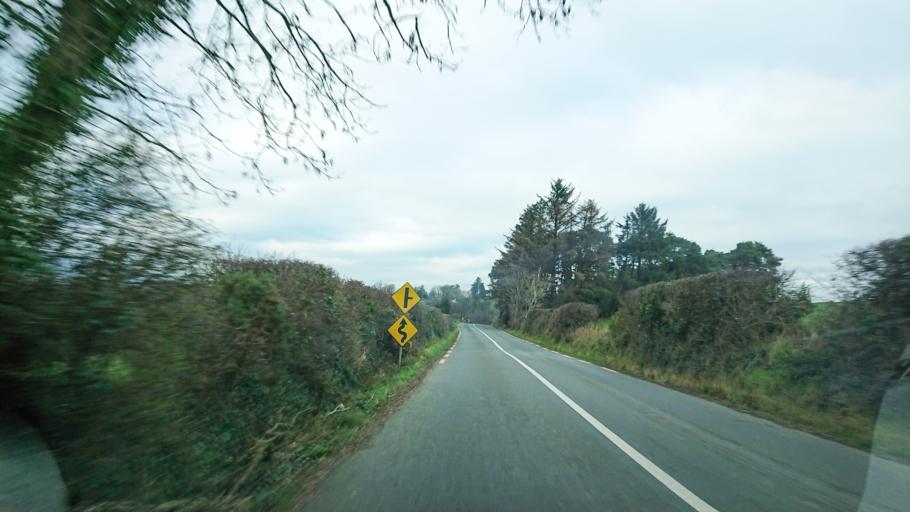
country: IE
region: Munster
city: Carrick-on-Suir
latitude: 52.2988
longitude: -7.4774
